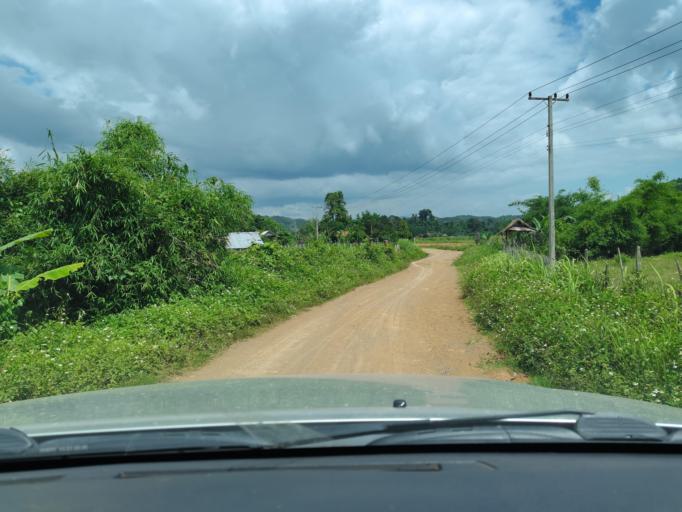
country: LA
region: Loungnamtha
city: Muang Long
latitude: 20.6828
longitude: 101.0506
